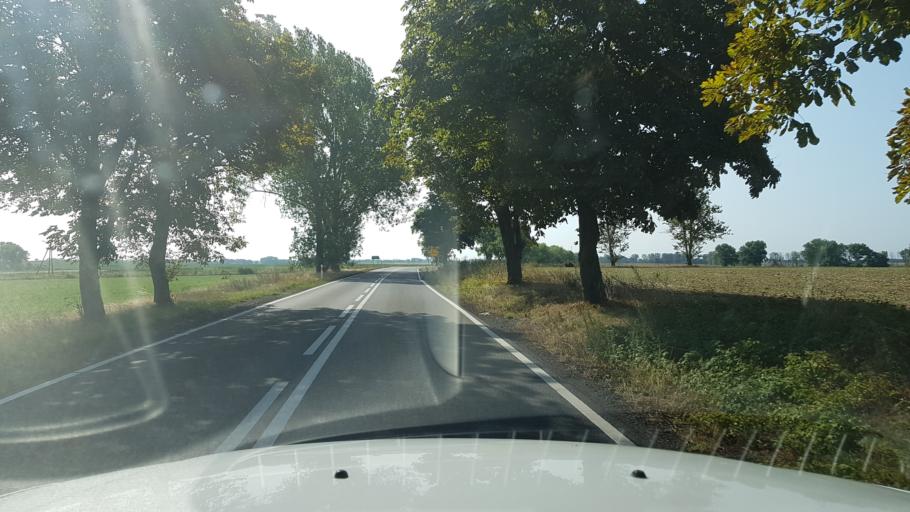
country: PL
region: West Pomeranian Voivodeship
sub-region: Powiat stargardzki
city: Stargard Szczecinski
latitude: 53.2610
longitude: 15.0974
